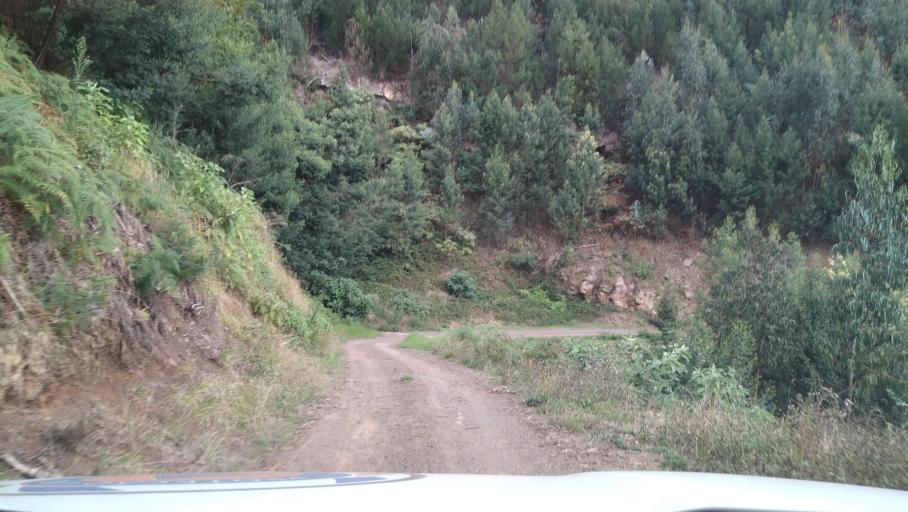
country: PT
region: Madeira
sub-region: Funchal
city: Nossa Senhora do Monte
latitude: 32.6829
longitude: -16.9244
